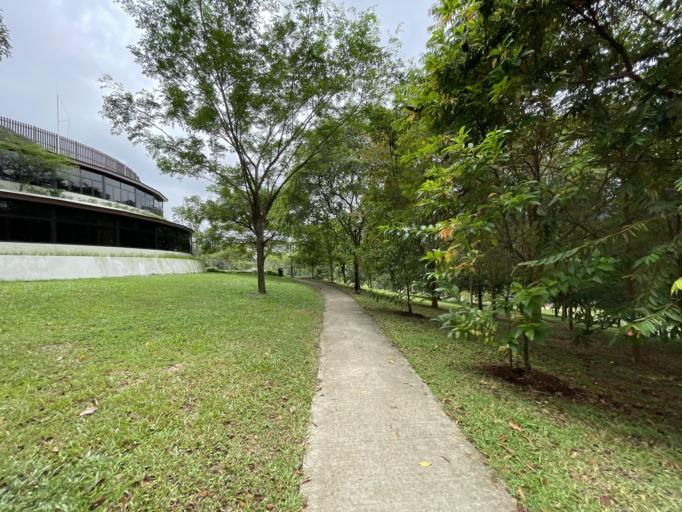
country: SG
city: Singapore
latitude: 1.3001
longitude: 103.7679
